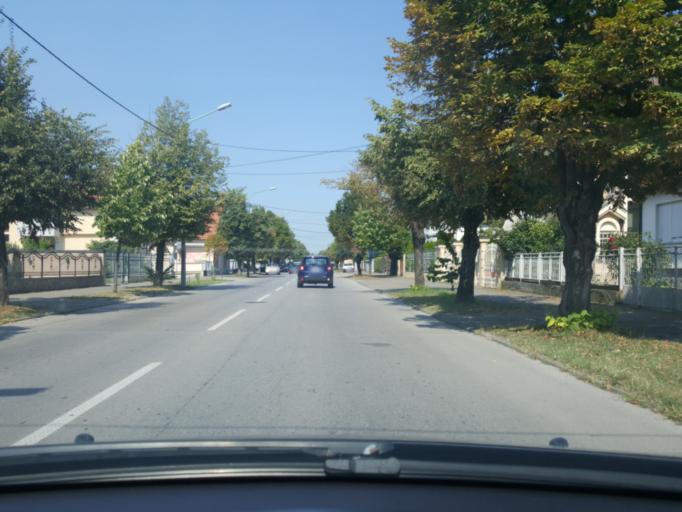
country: RS
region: Central Serbia
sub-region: Macvanski Okrug
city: Sabac
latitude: 44.7409
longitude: 19.6940
